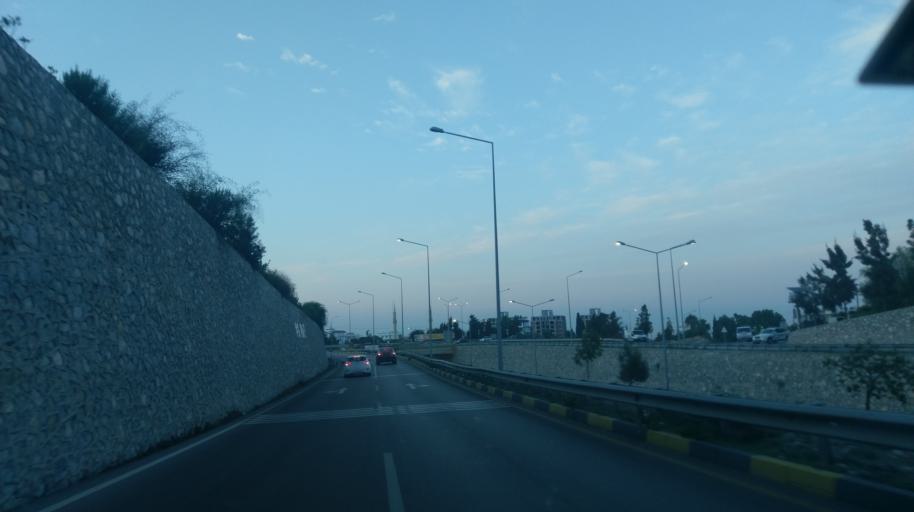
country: CY
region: Keryneia
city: Kyrenia
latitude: 35.3236
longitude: 33.3179
